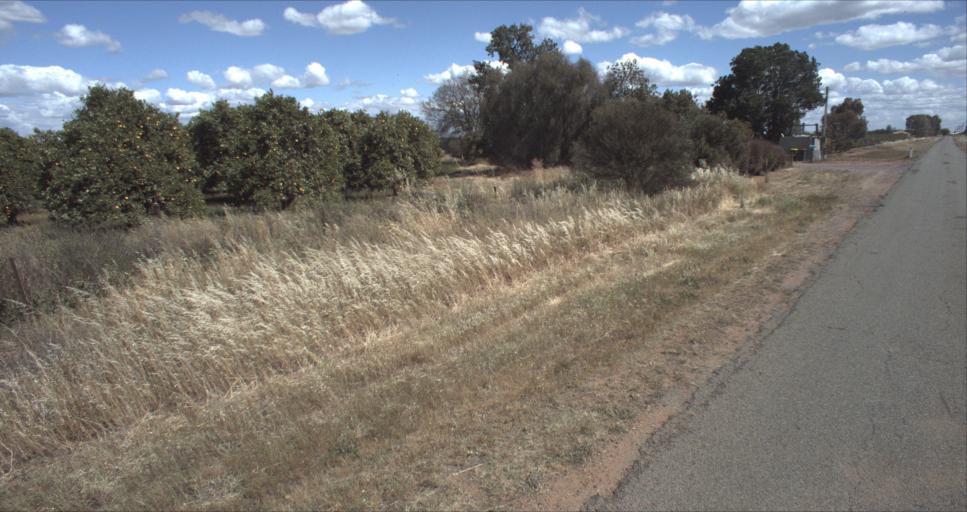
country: AU
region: New South Wales
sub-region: Leeton
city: Leeton
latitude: -34.5131
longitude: 146.2412
